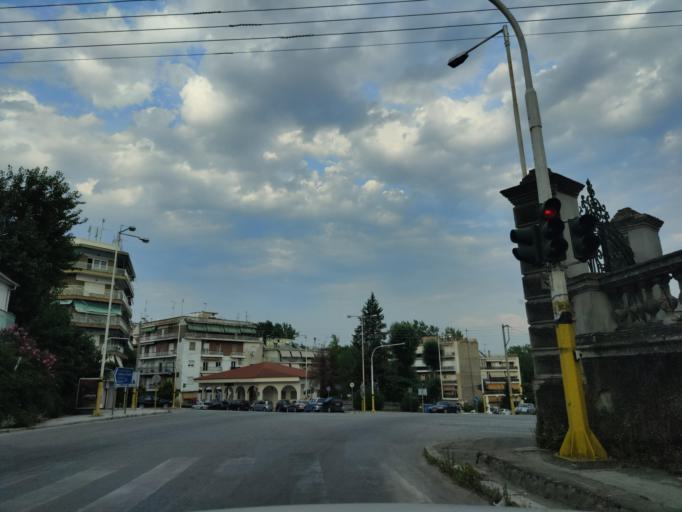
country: GR
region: East Macedonia and Thrace
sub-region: Nomos Dramas
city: Drama
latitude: 41.1497
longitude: 24.1385
